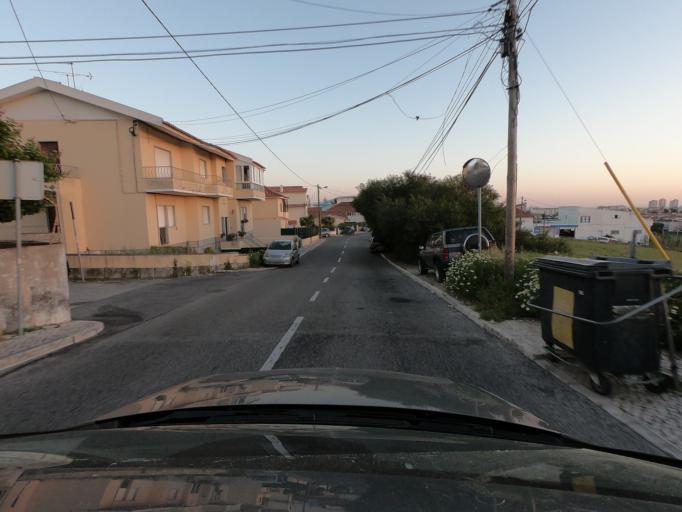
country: PT
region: Lisbon
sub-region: Cascais
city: Sao Domingos de Rana
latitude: 38.7043
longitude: -9.3291
